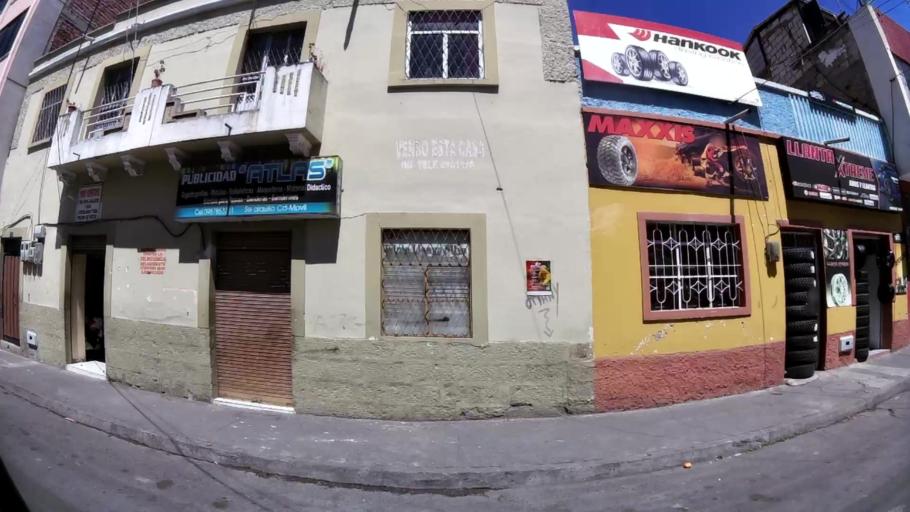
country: EC
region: Chimborazo
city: Riobamba
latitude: -1.6676
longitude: -78.6495
